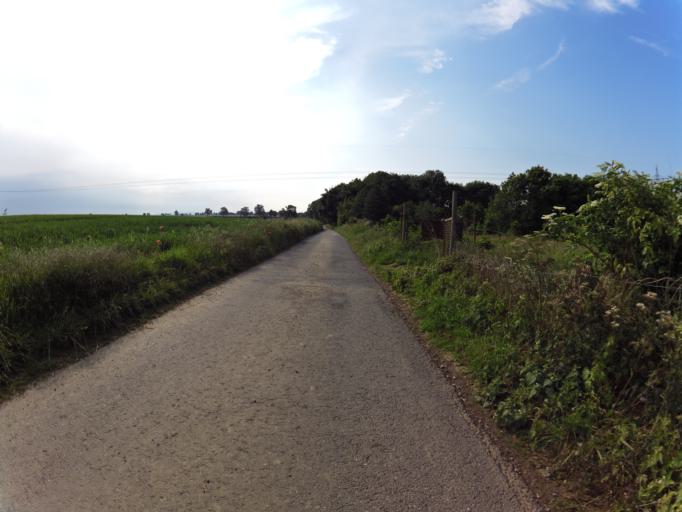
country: DE
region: North Rhine-Westphalia
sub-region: Regierungsbezirk Koln
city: Linnich
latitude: 50.9679
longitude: 6.2115
